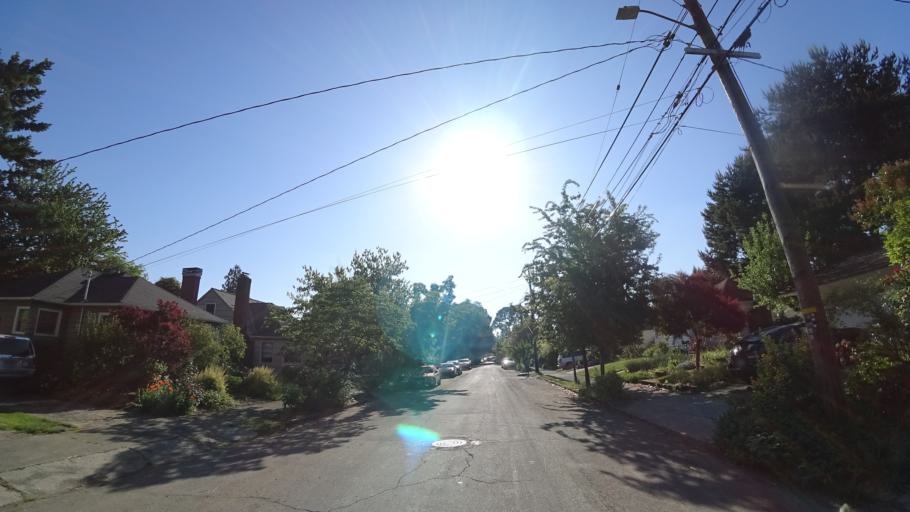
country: US
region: Oregon
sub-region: Multnomah County
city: Portland
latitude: 45.5765
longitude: -122.6644
